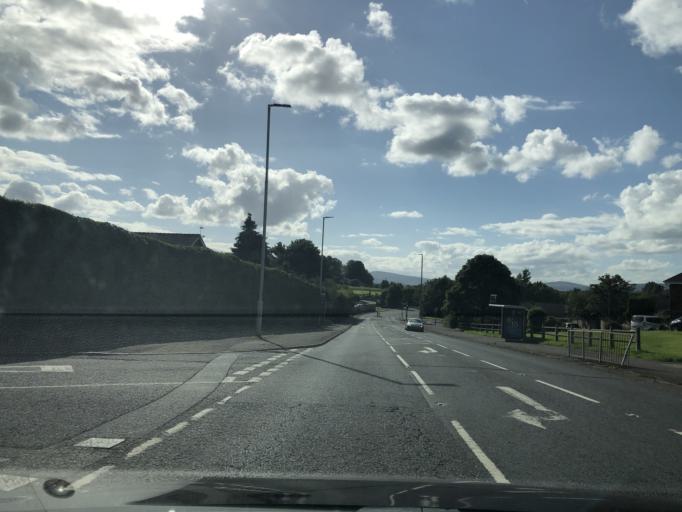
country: GB
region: Northern Ireland
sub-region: Castlereagh District
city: Dundonald
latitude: 54.5872
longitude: -5.8127
